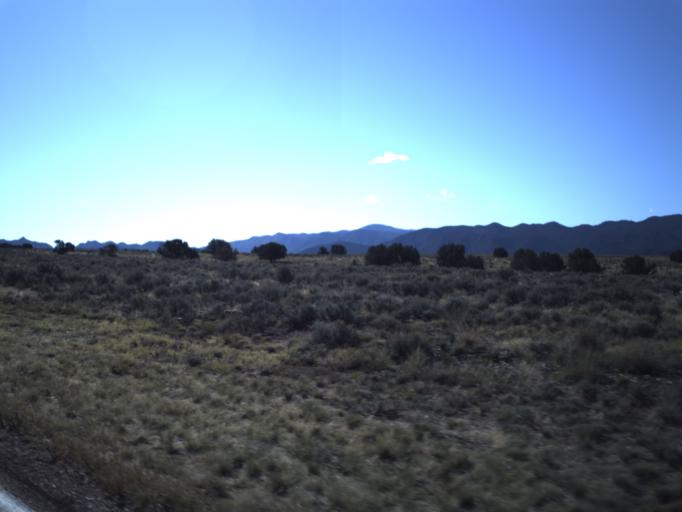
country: US
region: Utah
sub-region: Washington County
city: Enterprise
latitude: 37.6701
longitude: -113.4837
